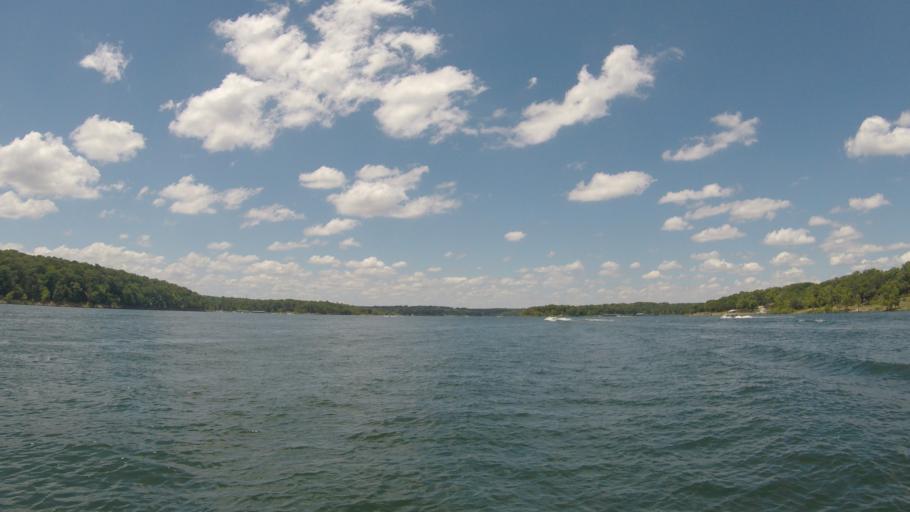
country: US
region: Missouri
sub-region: Barry County
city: Shell Knob
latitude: 36.5894
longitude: -93.5551
